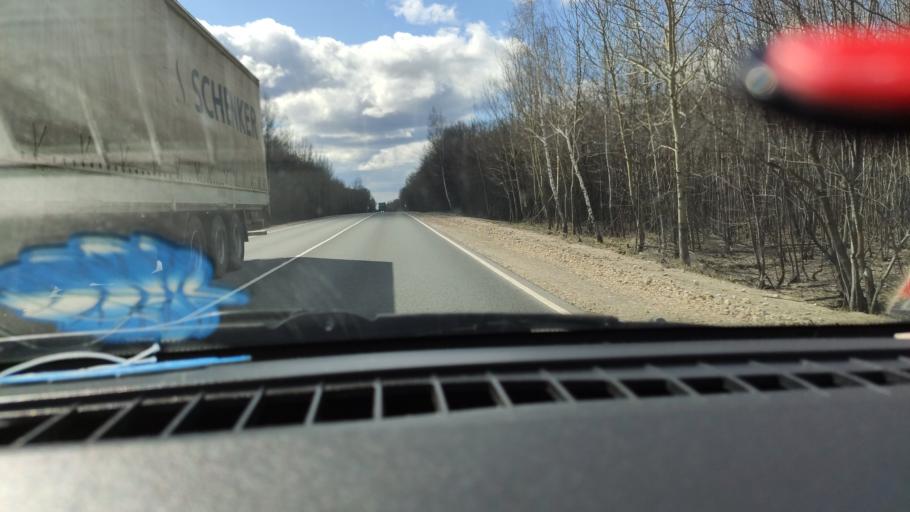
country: RU
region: Saratov
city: Khvalynsk
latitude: 52.4484
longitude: 48.0109
